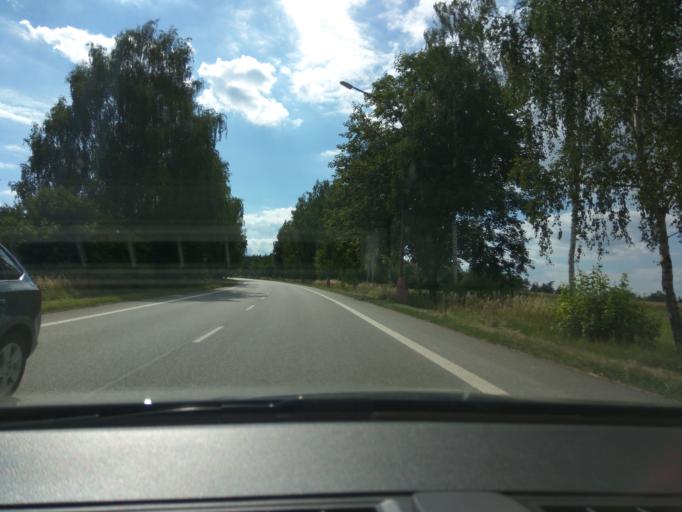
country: CZ
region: Jihocesky
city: Cimelice
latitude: 49.5031
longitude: 14.1644
